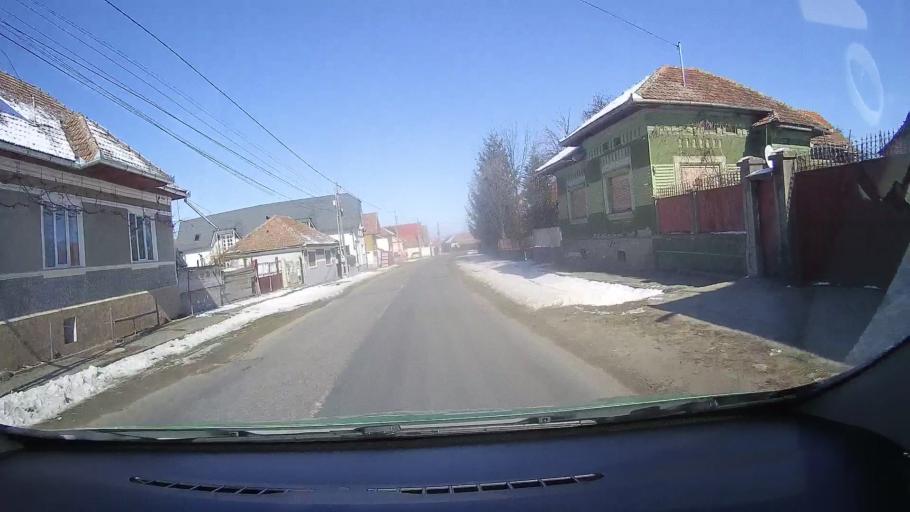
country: RO
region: Brasov
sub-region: Oras Victoria
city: Victoria
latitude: 45.7474
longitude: 24.7394
